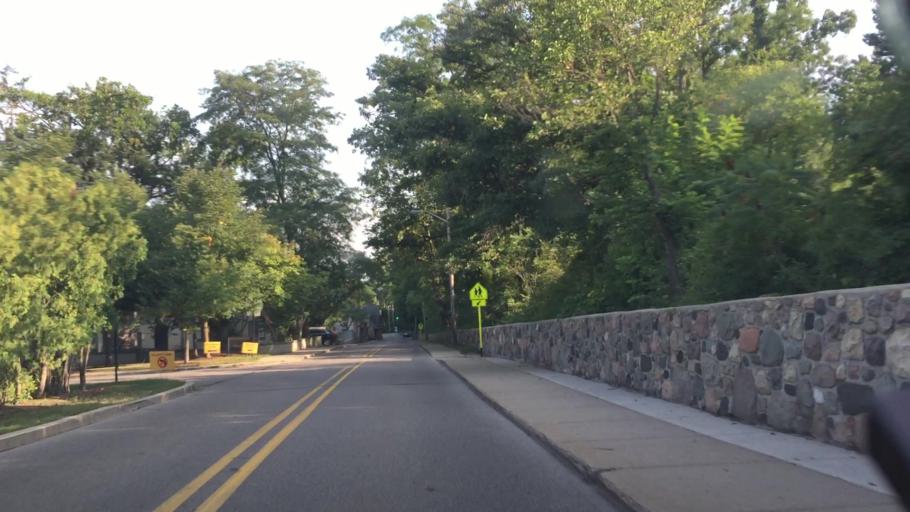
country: US
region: Michigan
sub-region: Oakland County
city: Bloomfield Hills
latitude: 42.5699
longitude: -83.2433
